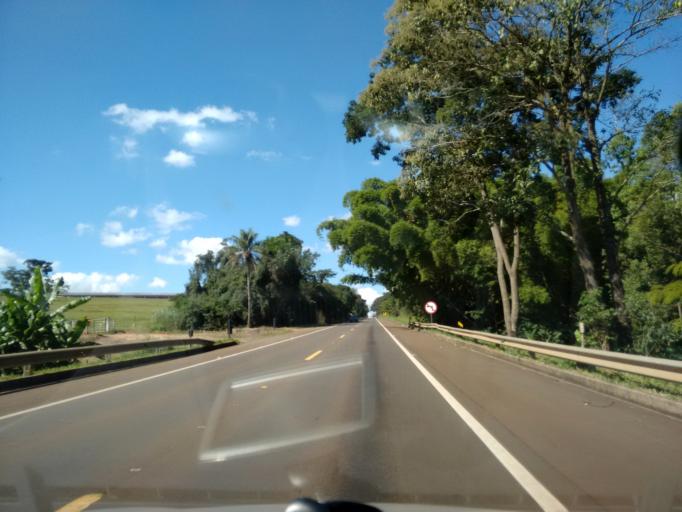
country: BR
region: Sao Paulo
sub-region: Ribeirao Bonito
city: Ribeirao Bonito
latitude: -22.0848
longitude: -48.1642
